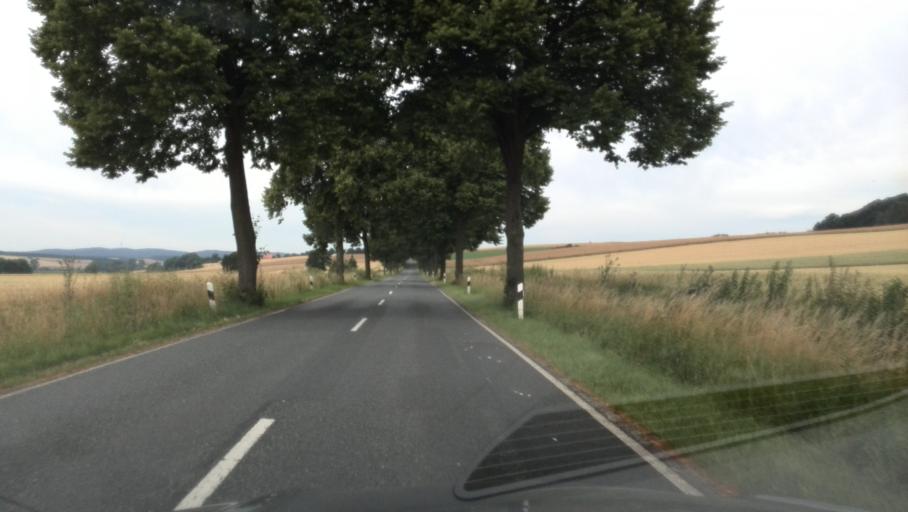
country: DE
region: Lower Saxony
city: Holle
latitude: 52.1064
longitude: 10.0942
